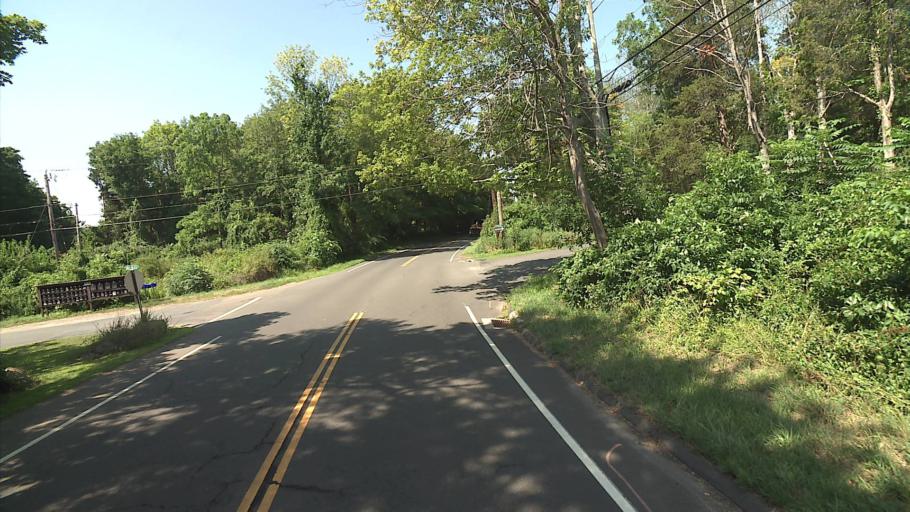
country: US
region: Connecticut
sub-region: New Haven County
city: Guilford
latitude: 41.2644
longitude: -72.7174
